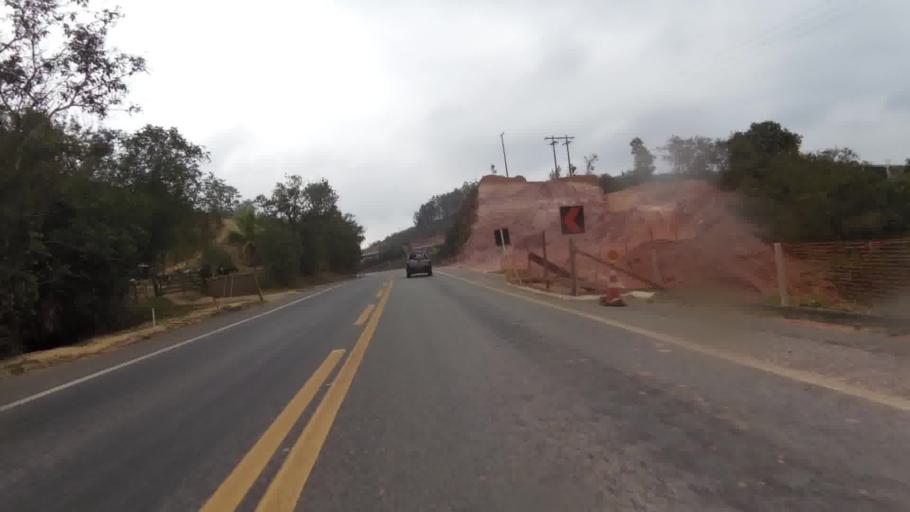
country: BR
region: Espirito Santo
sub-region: Rio Novo Do Sul
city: Rio Novo do Sul
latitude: -20.8955
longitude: -41.0073
